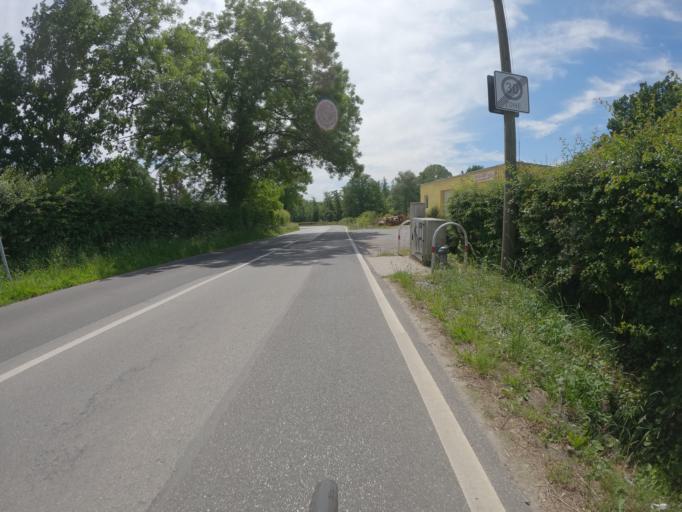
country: DE
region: North Rhine-Westphalia
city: Stolberg
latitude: 50.7393
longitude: 6.1557
